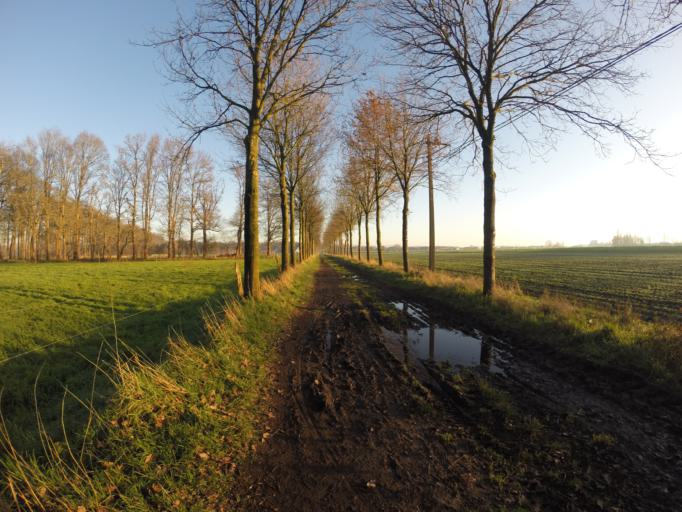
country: BE
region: Flanders
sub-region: Provincie West-Vlaanderen
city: Wingene
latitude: 51.0871
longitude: 3.2983
